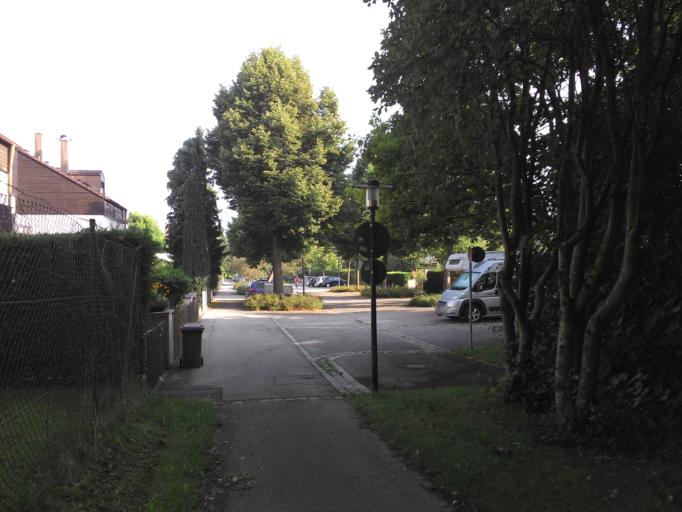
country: DE
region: Bavaria
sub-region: Upper Bavaria
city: Grafelfing
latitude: 48.1471
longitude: 11.4181
